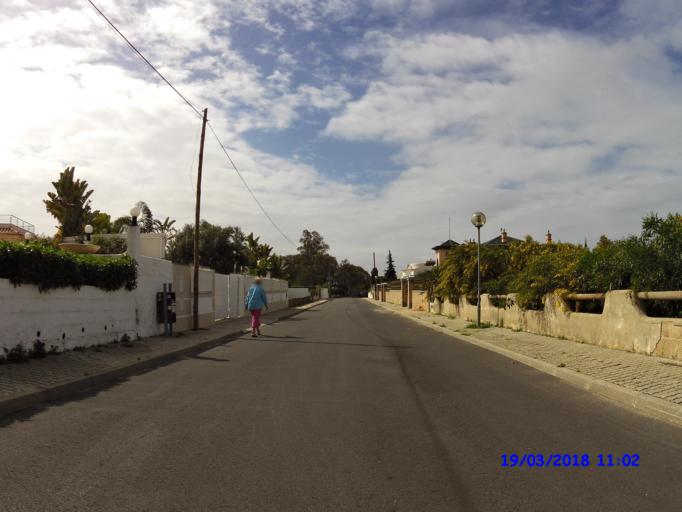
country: PT
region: Faro
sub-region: Albufeira
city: Albufeira
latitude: 37.0792
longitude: -8.2990
